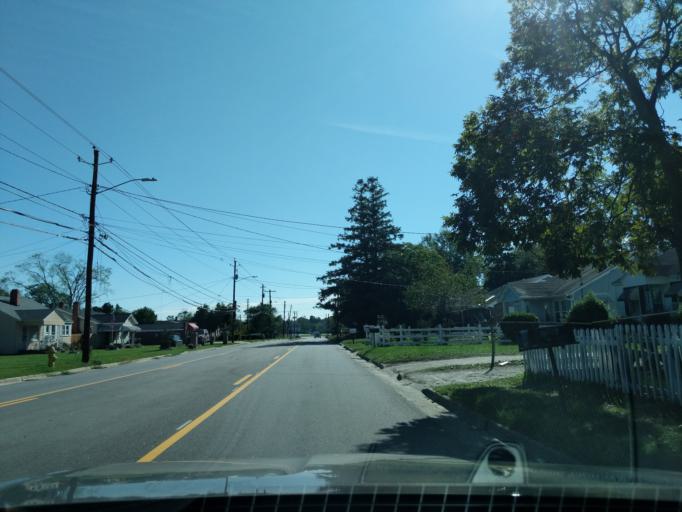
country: US
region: Georgia
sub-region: Richmond County
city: Augusta
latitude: 33.4414
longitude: -82.0008
